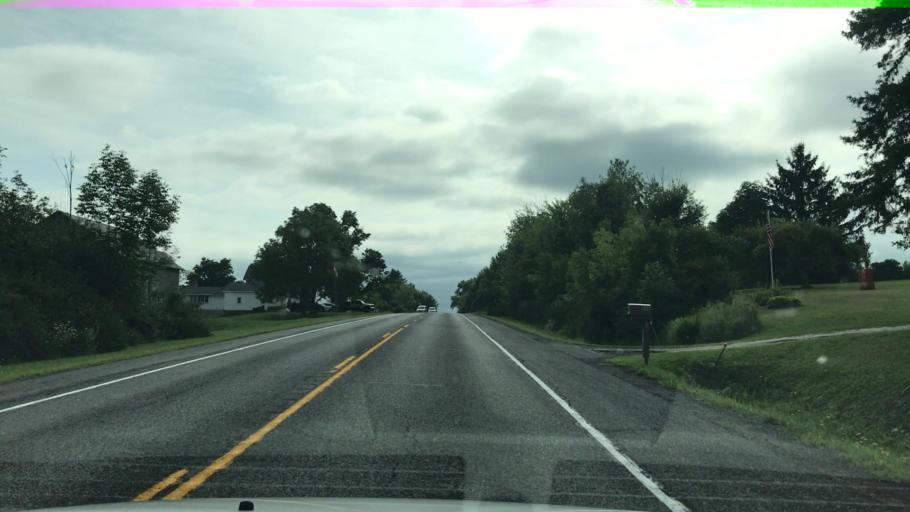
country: US
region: New York
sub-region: Erie County
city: Alden
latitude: 42.8350
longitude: -78.4412
